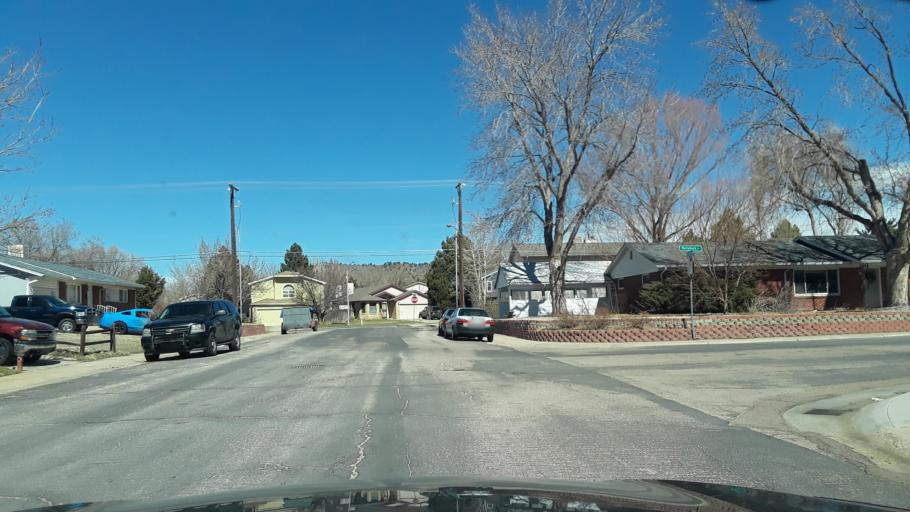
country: US
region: Colorado
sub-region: El Paso County
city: Colorado Springs
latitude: 38.8781
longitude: -104.8007
